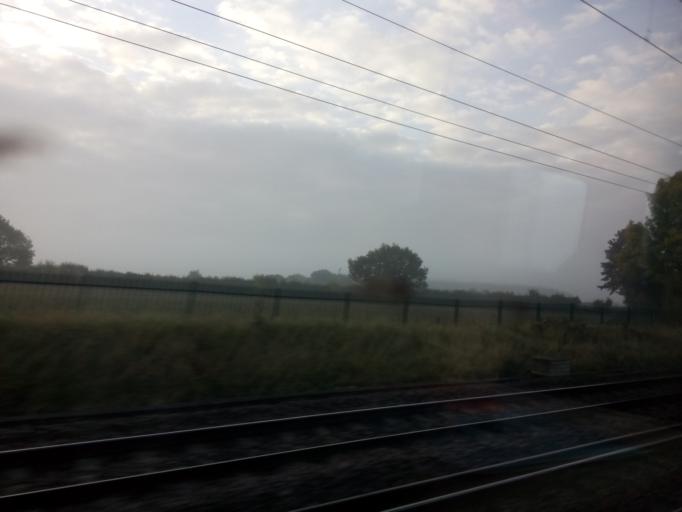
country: GB
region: England
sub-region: City of York
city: Copmanthorpe
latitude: 53.9053
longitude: -1.1475
